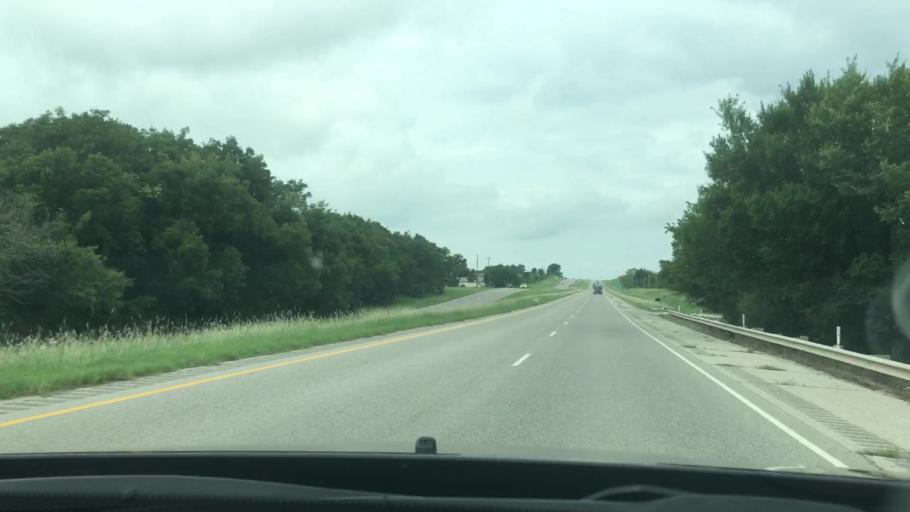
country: US
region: Oklahoma
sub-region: Carter County
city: Wilson
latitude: 34.1731
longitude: -97.4516
